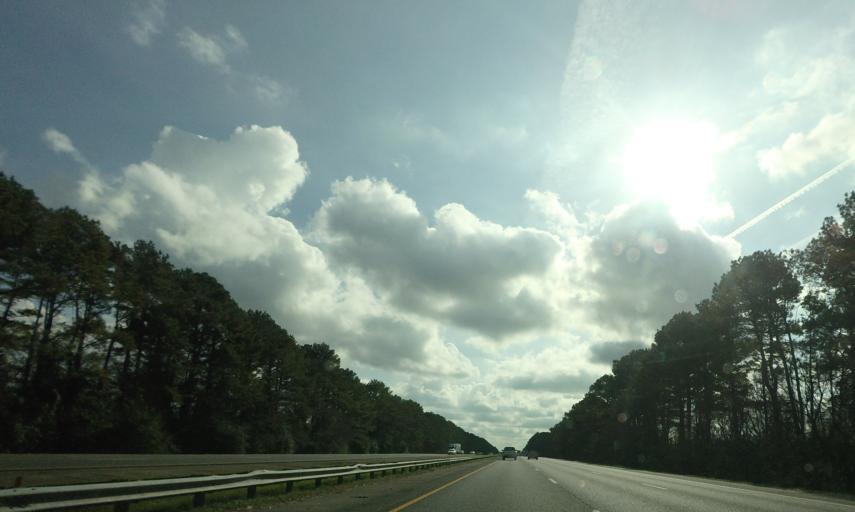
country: US
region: Georgia
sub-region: Houston County
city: Perry
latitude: 32.5095
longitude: -83.7431
